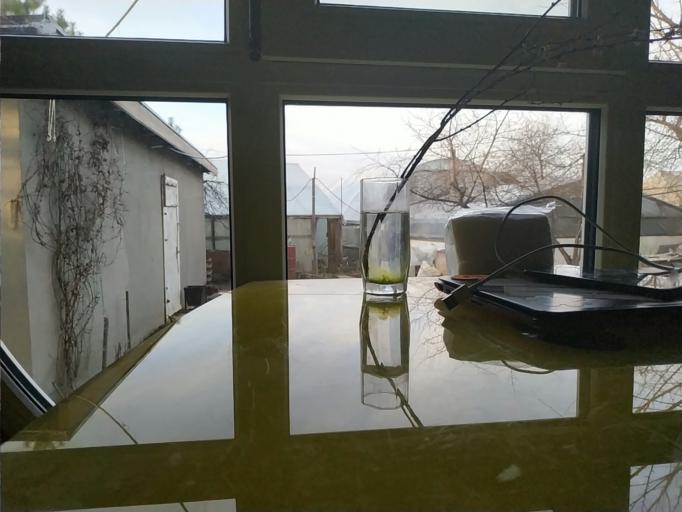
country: RU
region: Republic of Karelia
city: Suoyarvi
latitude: 62.2717
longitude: 32.0855
